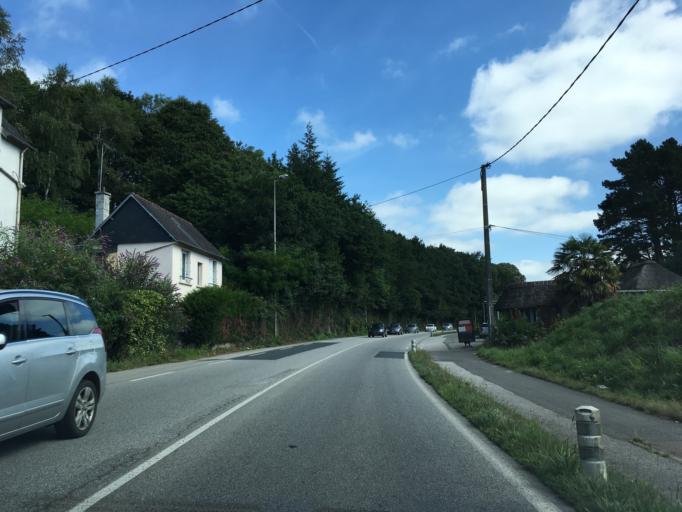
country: FR
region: Brittany
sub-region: Departement du Finistere
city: Quimper
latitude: 48.0080
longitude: -4.0830
